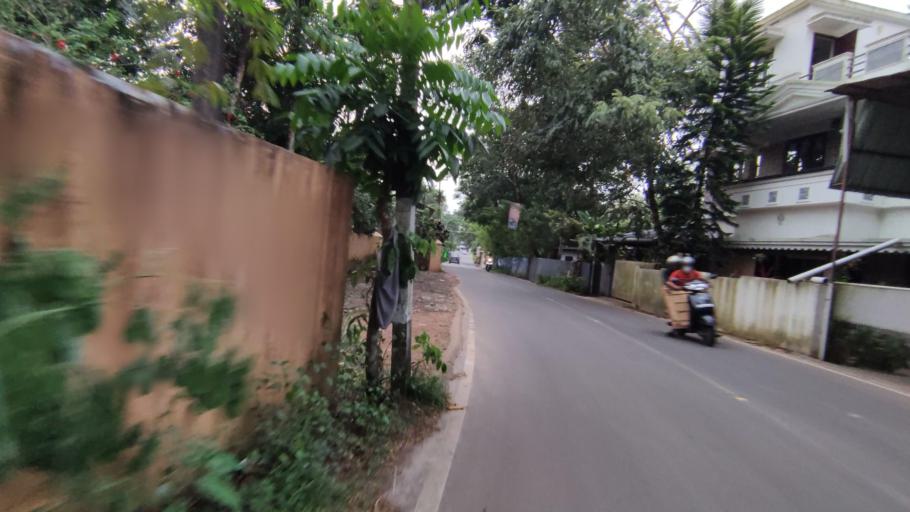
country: IN
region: Kerala
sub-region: Alappuzha
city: Shertallai
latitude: 9.6560
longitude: 76.3690
